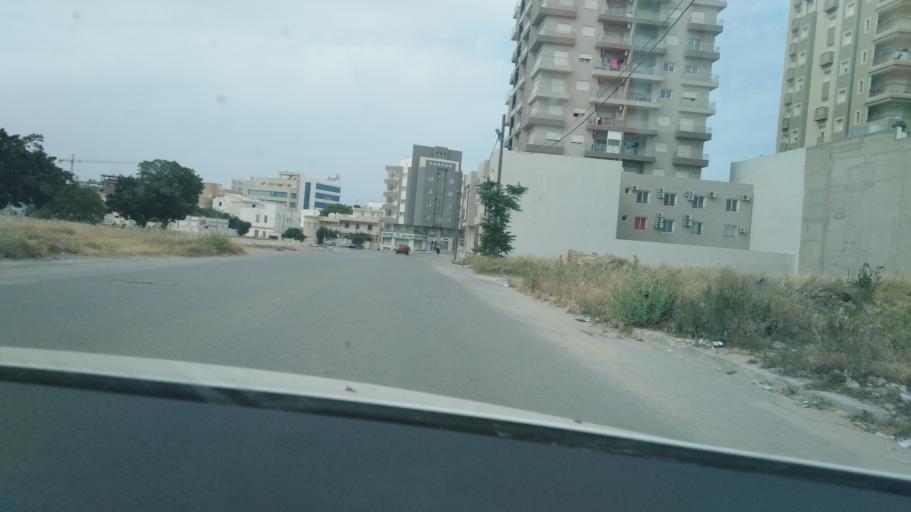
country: TN
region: Susah
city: Sousse
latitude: 35.8257
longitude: 10.6323
